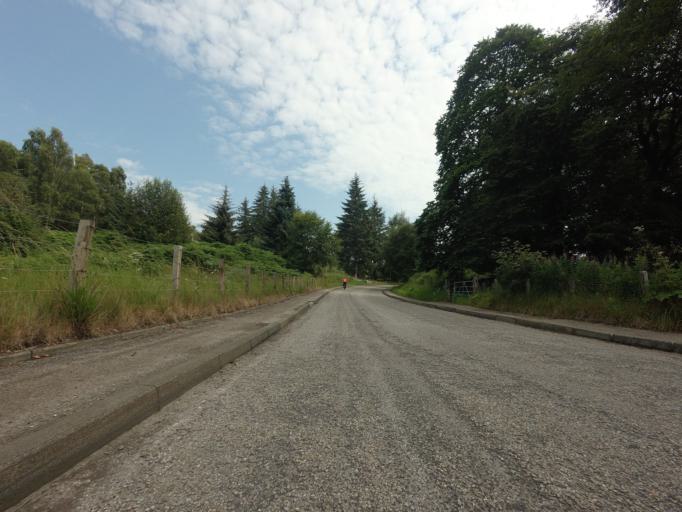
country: GB
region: Scotland
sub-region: Highland
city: Evanton
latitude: 57.9441
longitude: -4.4086
